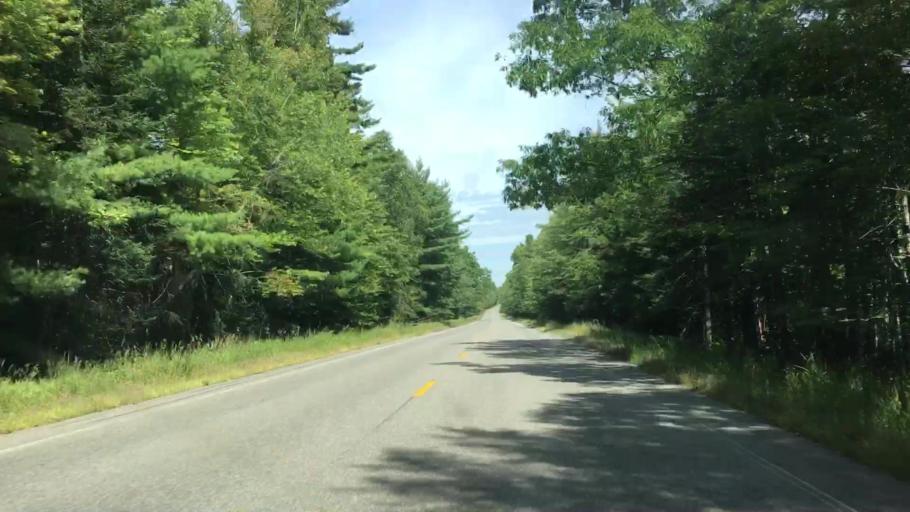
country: US
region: Maine
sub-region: Penobscot County
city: Lincoln
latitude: 45.3830
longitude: -68.5432
